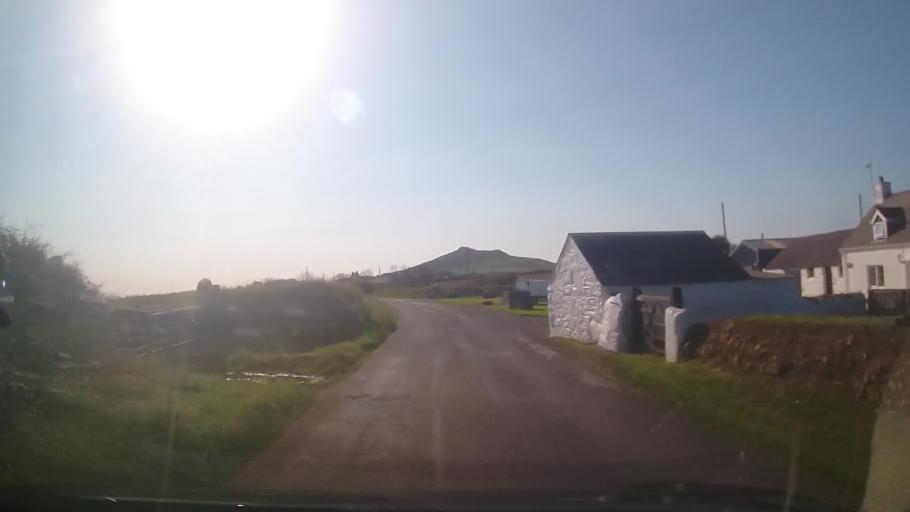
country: GB
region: Wales
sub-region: Pembrokeshire
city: Saint David's
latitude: 51.9194
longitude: -5.2302
